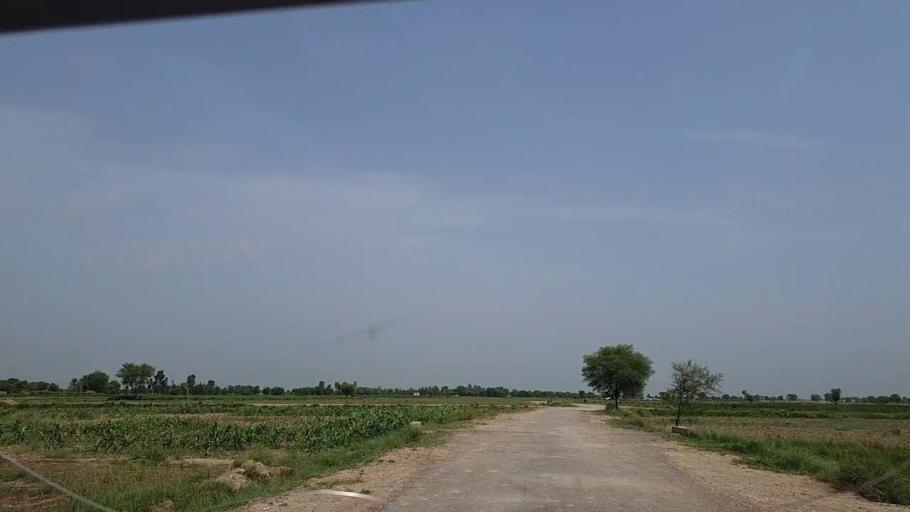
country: PK
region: Sindh
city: Tharu Shah
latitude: 26.9111
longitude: 68.0530
